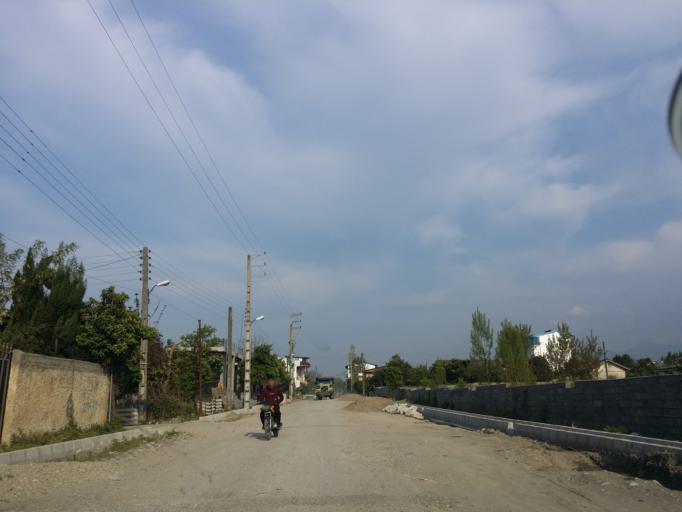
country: IR
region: Mazandaran
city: Chalus
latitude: 36.6575
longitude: 51.3929
